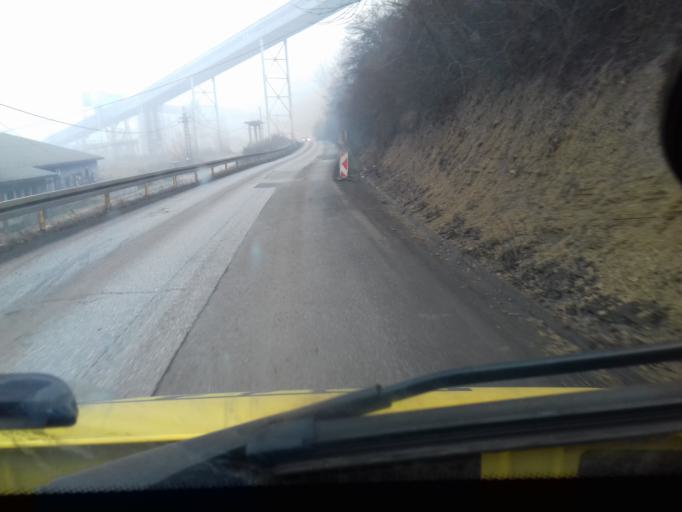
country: BA
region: Federation of Bosnia and Herzegovina
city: Kakanj
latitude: 44.1035
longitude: 18.1135
